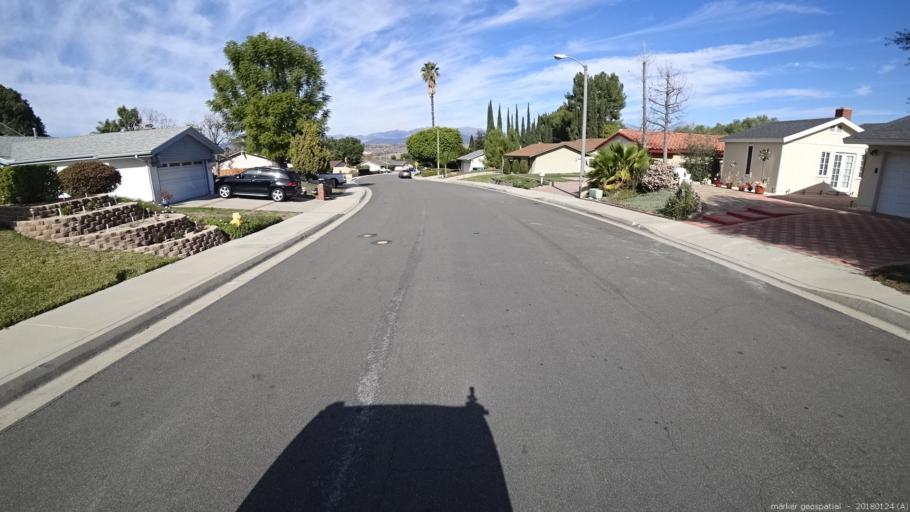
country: US
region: California
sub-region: Los Angeles County
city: Diamond Bar
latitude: 34.0256
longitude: -117.8136
